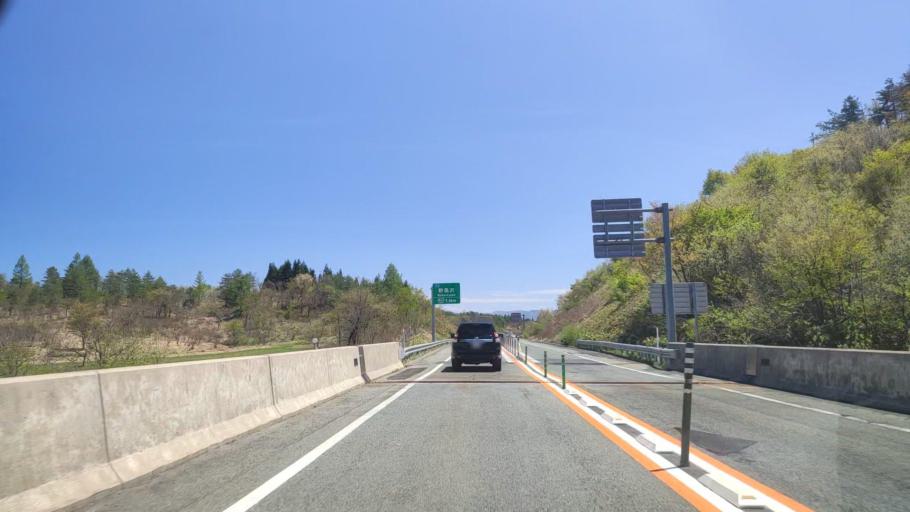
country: JP
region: Yamagata
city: Obanazawa
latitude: 38.6532
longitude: 140.3687
